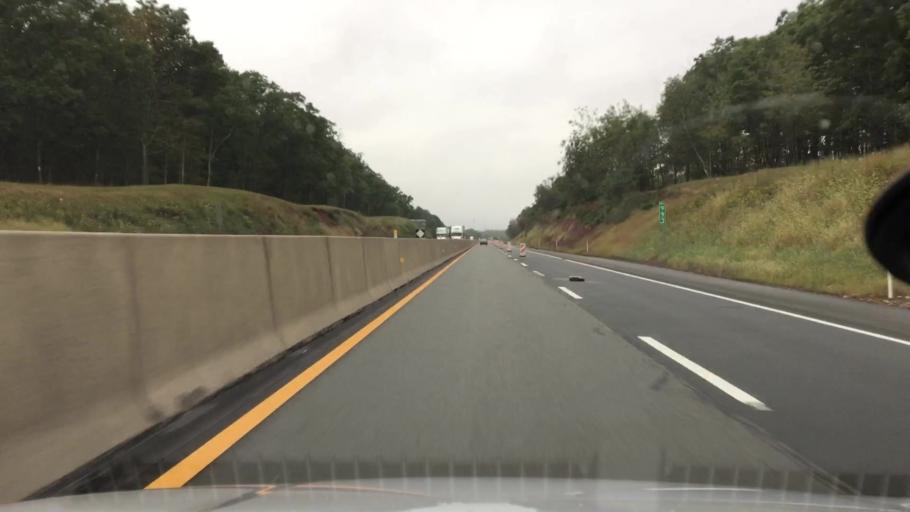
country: US
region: Pennsylvania
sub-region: Luzerne County
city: White Haven
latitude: 41.1175
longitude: -75.7649
